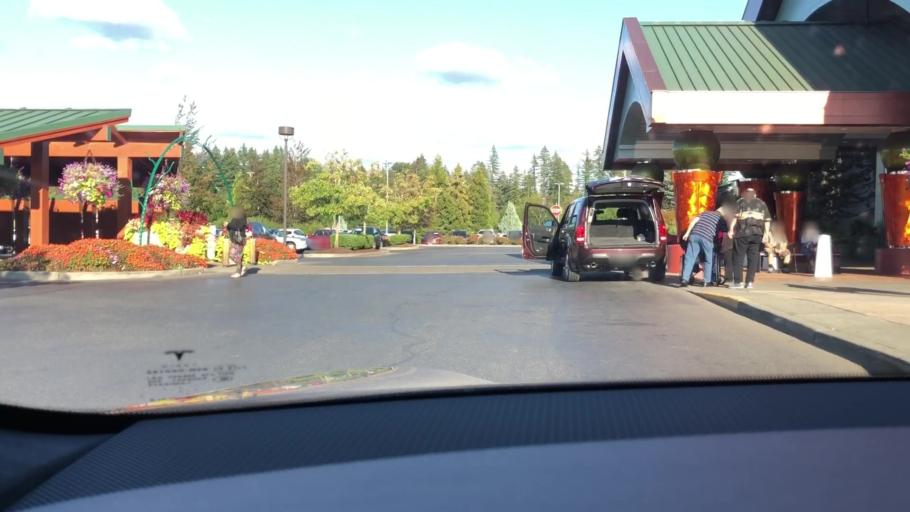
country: US
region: Washington
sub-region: Snohomish County
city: Marysville
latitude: 48.0888
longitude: -122.1897
